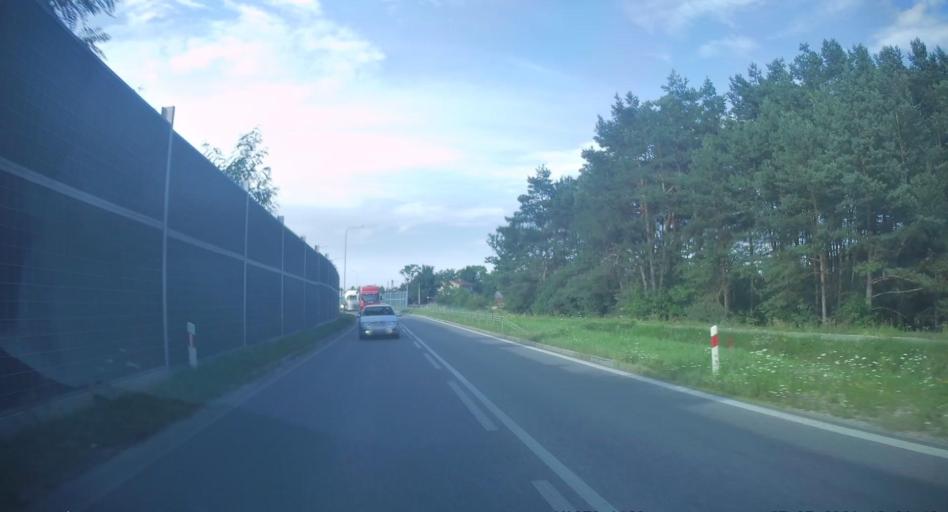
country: PL
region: Swietokrzyskie
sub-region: Powiat konecki
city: Konskie
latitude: 51.1277
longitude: 20.3593
